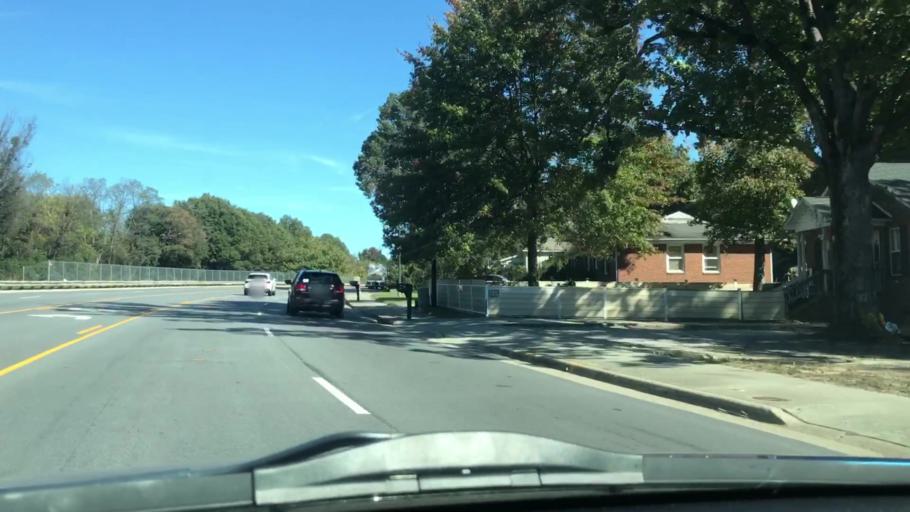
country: US
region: North Carolina
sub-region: Guilford County
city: High Point
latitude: 35.9659
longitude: -79.9830
